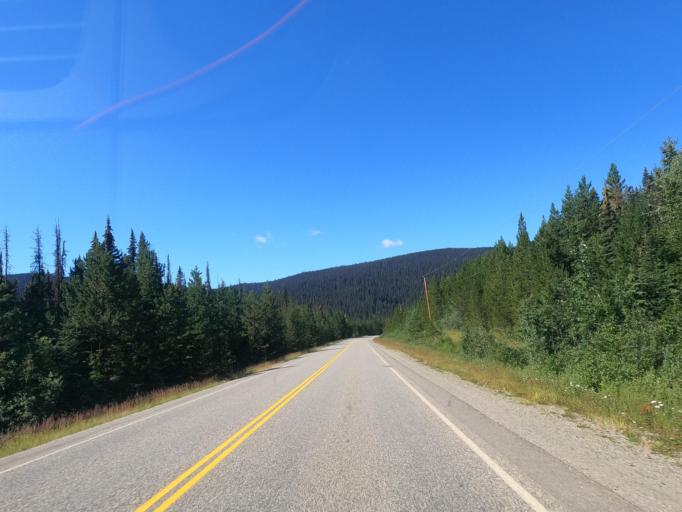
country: CA
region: British Columbia
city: Quesnel
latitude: 53.0457
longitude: -121.7137
